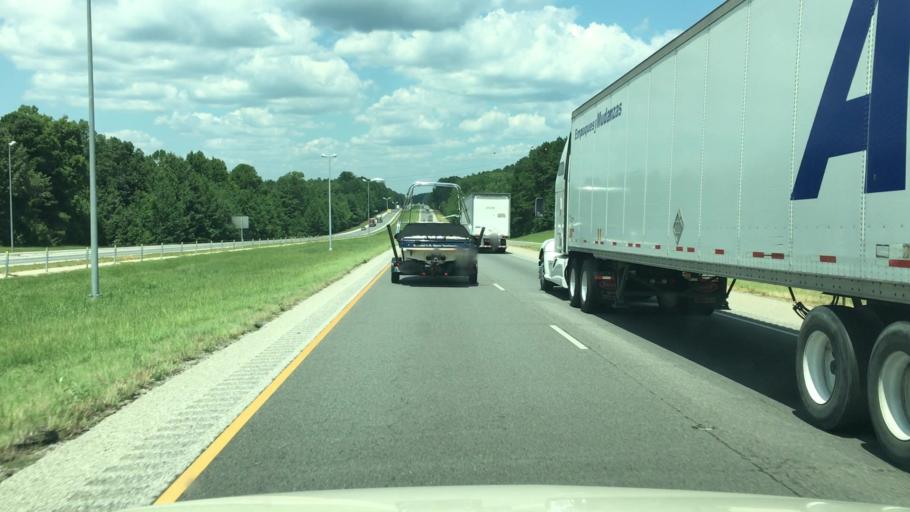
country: US
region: Arkansas
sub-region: Clark County
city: Arkadelphia
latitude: 34.1212
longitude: -93.0914
